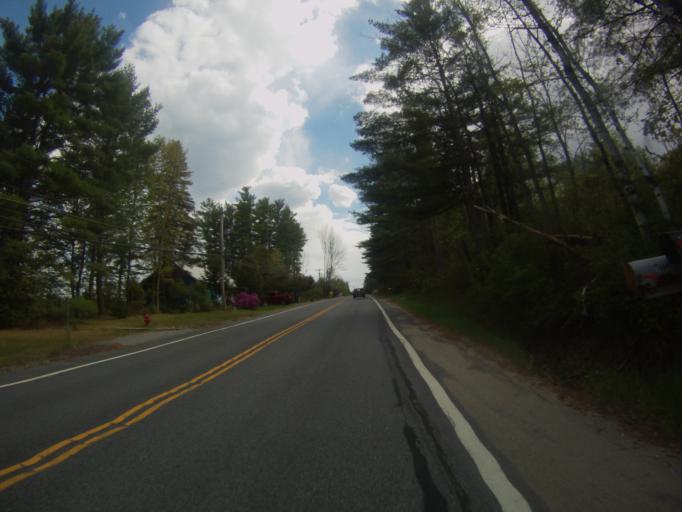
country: US
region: New York
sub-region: Essex County
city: Mineville
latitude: 43.8692
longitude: -73.7526
